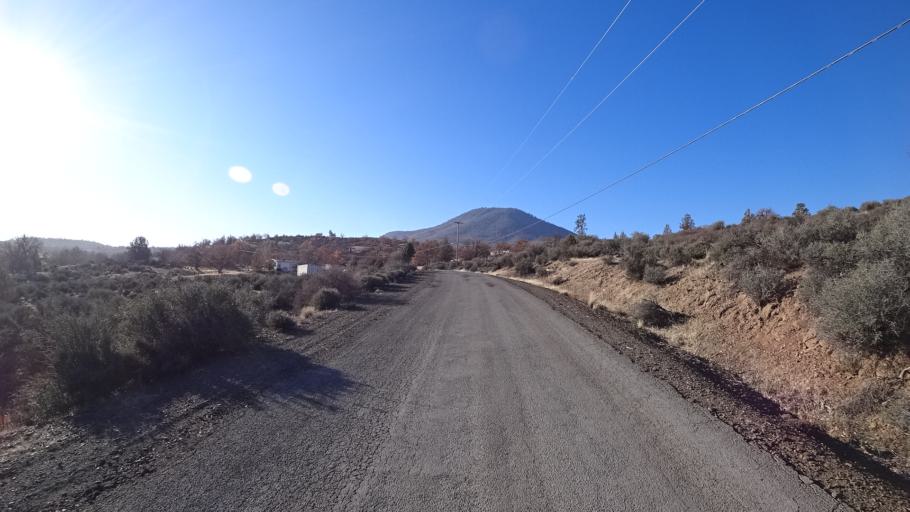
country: US
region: California
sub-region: Siskiyou County
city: Montague
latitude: 41.8949
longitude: -122.4966
